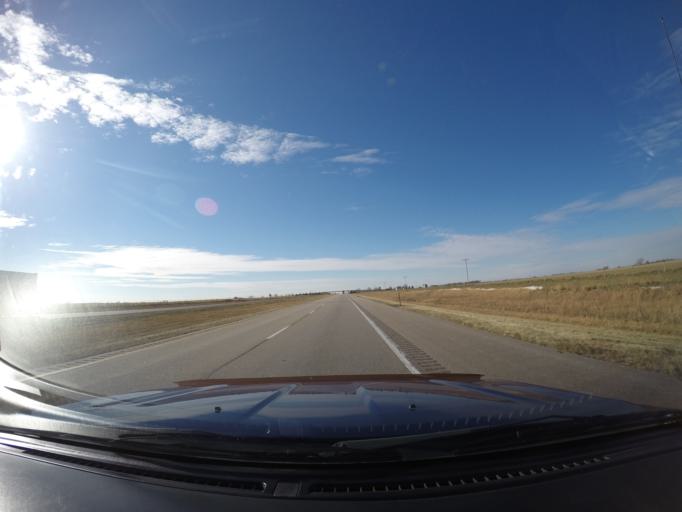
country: US
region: Nebraska
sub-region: York County
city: York
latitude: 40.8214
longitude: -97.6817
